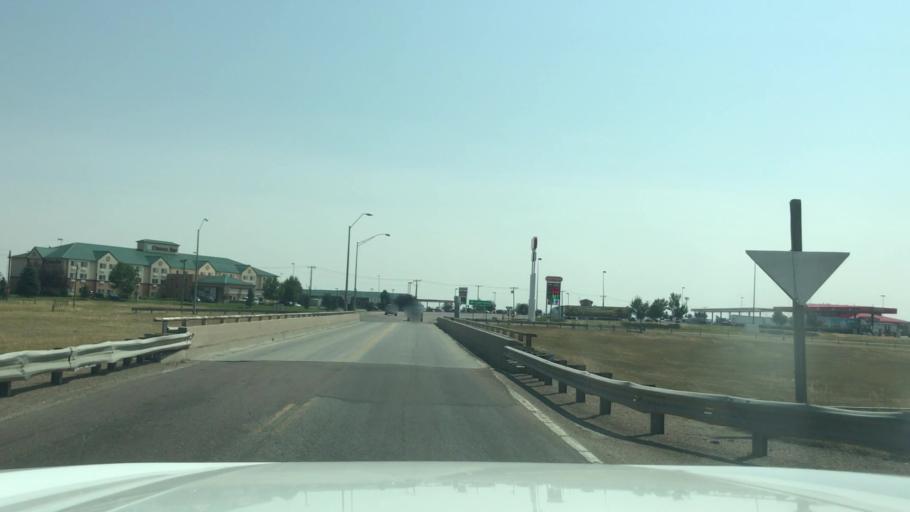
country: US
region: Montana
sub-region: Cascade County
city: Great Falls
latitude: 47.4727
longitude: -111.3614
